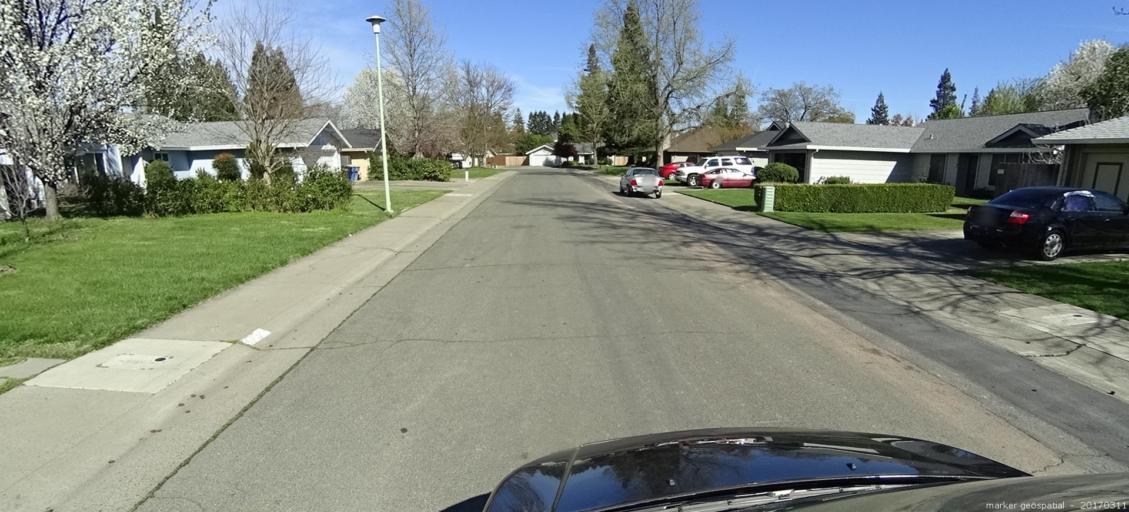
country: US
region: California
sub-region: Sacramento County
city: Parkway
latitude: 38.4913
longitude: -121.5474
